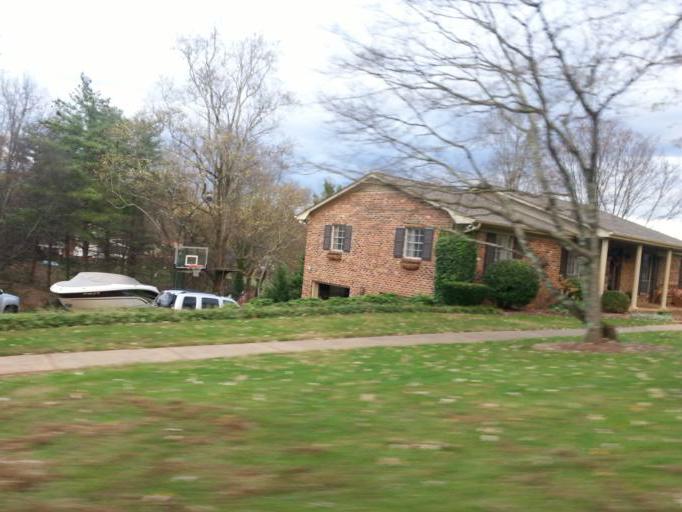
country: US
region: Tennessee
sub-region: Blount County
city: Louisville
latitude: 35.9139
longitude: -84.0456
